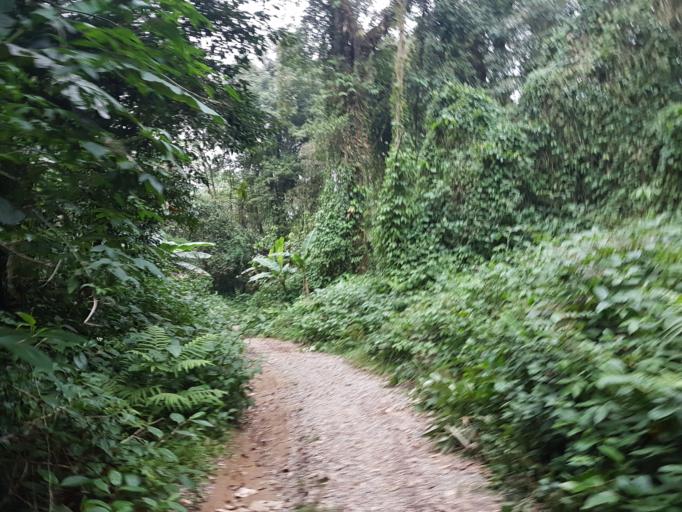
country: TH
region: Phetchabun
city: Lom Kao
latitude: 16.8936
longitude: 101.0948
